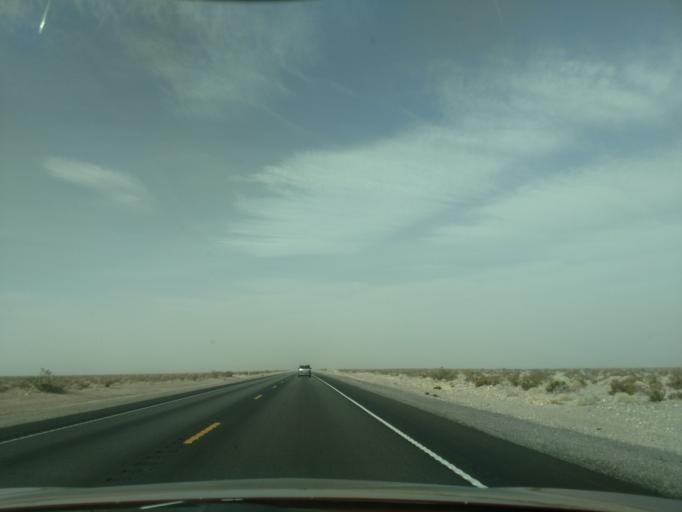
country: US
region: Nevada
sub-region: Nye County
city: Beatty
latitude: 36.6344
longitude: -116.3622
